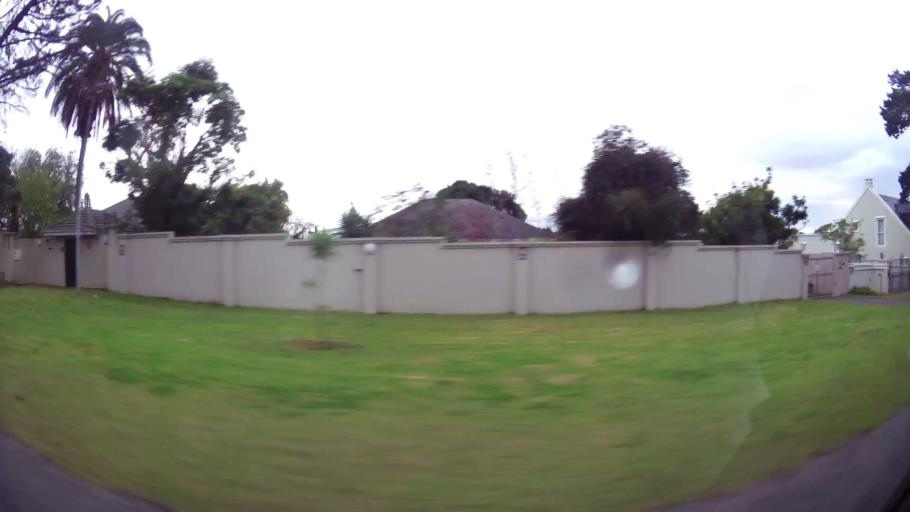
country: ZA
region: Eastern Cape
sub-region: Nelson Mandela Bay Metropolitan Municipality
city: Port Elizabeth
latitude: -33.9759
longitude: 25.5811
